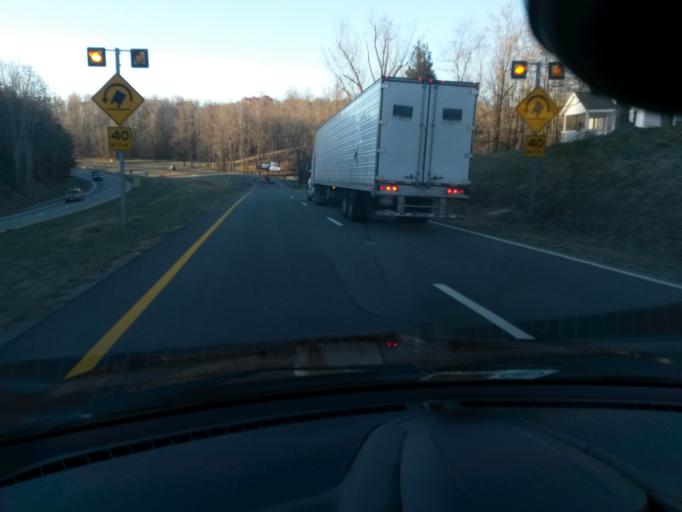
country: US
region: Virginia
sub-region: Franklin County
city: Henry Fork
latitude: 36.8814
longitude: -79.8698
